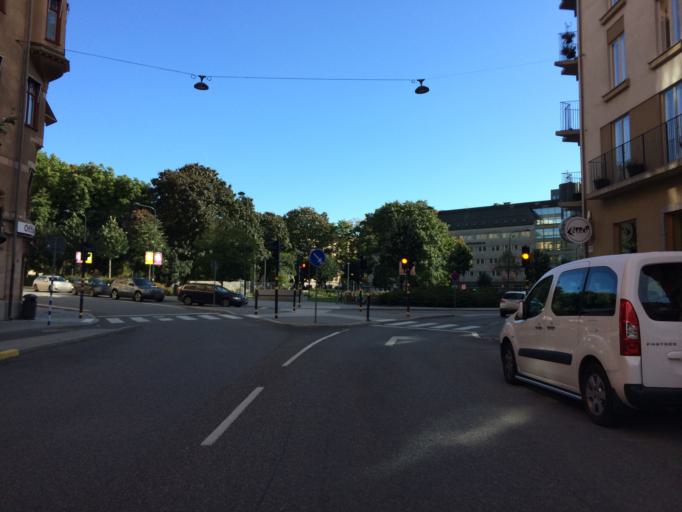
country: SE
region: Stockholm
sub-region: Stockholms Kommun
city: Stockholm
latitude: 59.3353
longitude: 18.0527
